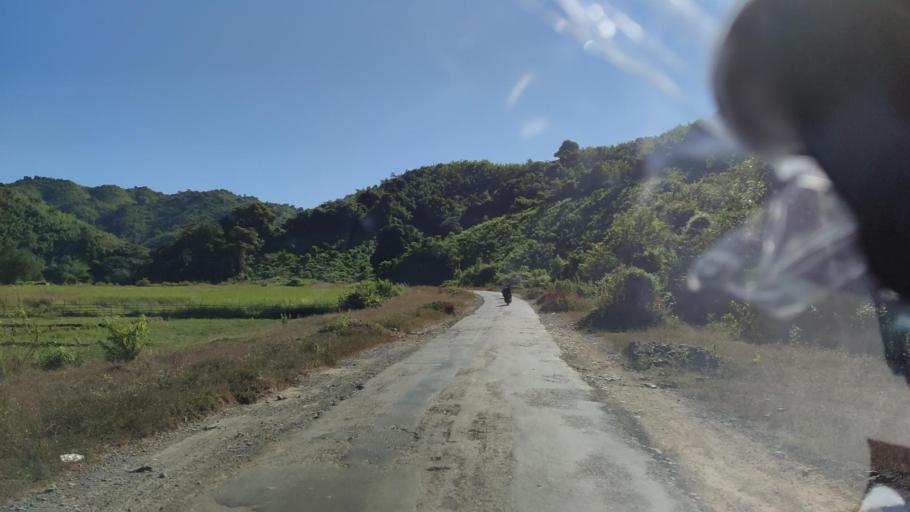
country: MM
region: Rakhine
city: Sittwe
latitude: 19.9688
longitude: 93.7286
